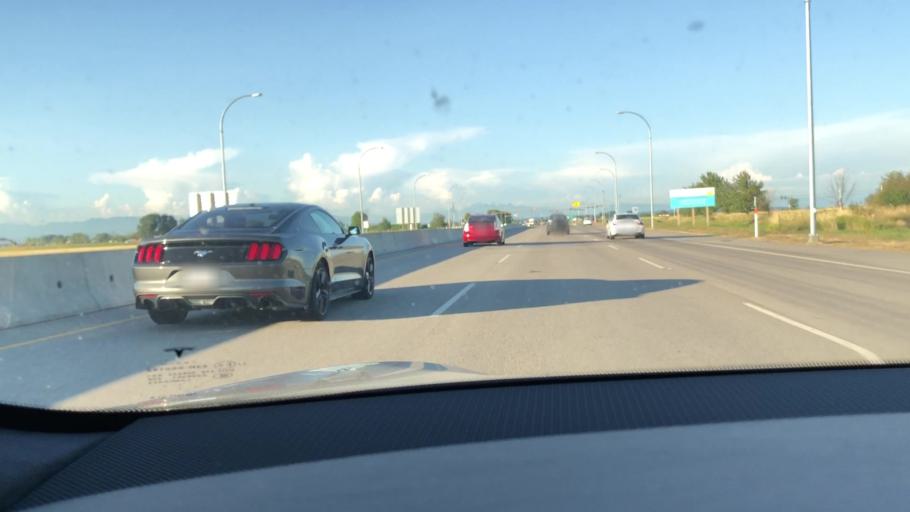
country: CA
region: British Columbia
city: Ladner
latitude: 49.0405
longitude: -123.0731
